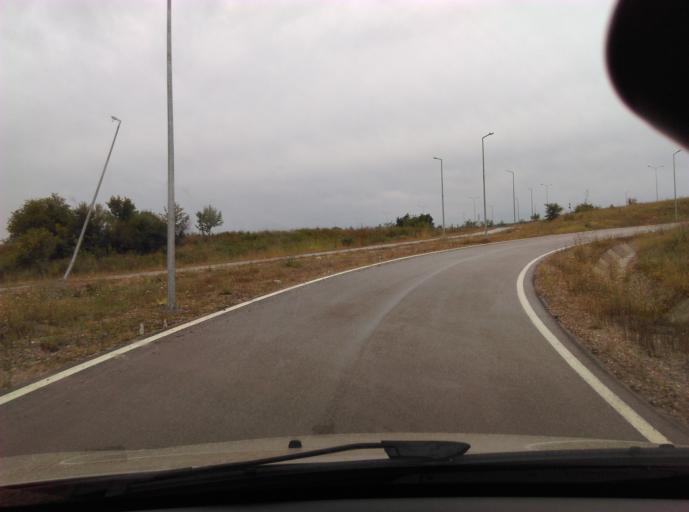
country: BG
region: Khaskovo
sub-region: Obshtina Dimitrovgrad
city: Dimitrovgrad
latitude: 42.0211
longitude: 25.5835
